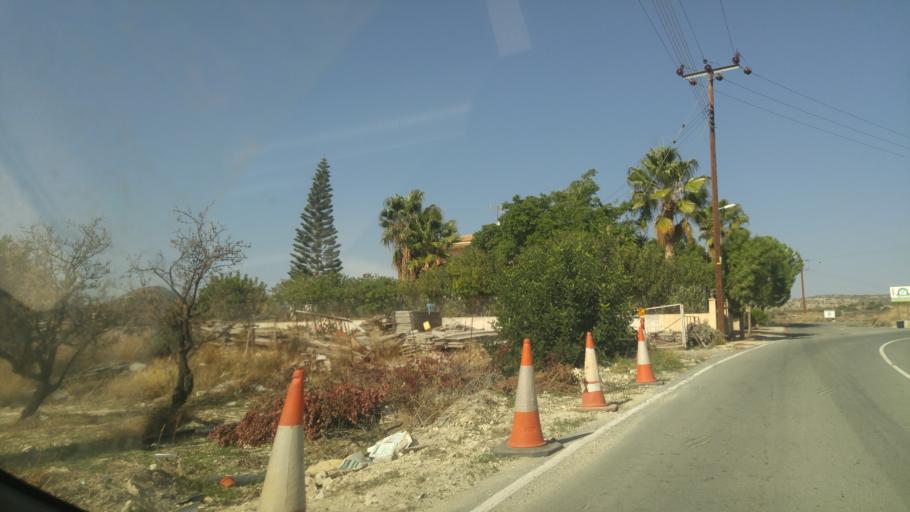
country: CY
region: Limassol
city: Pano Polemidia
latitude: 34.7388
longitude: 33.0254
